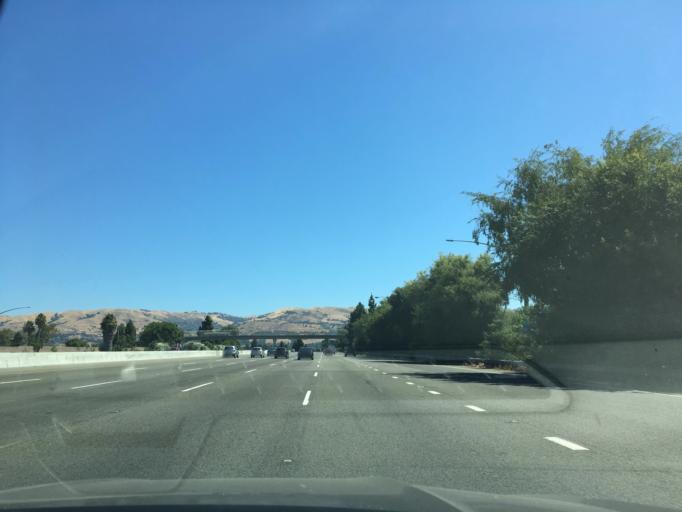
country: US
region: California
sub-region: Santa Clara County
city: Alum Rock
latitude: 37.3455
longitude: -121.8434
